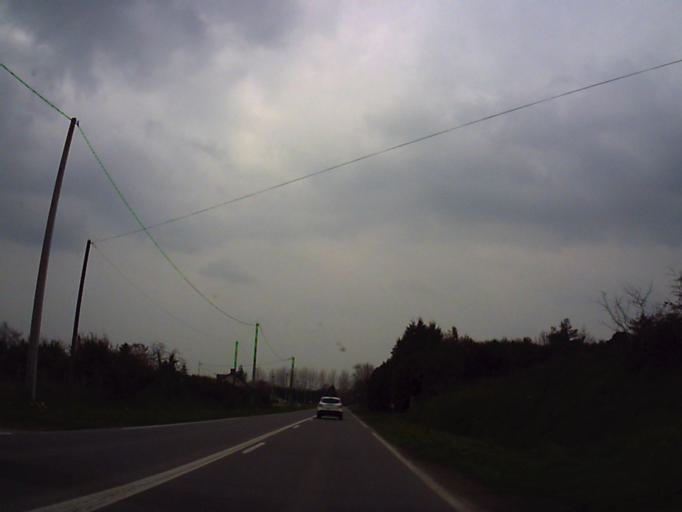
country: FR
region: Brittany
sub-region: Departement d'Ille-et-Vilaine
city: La Chapelle-Thouarault
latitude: 48.1381
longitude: -1.8698
